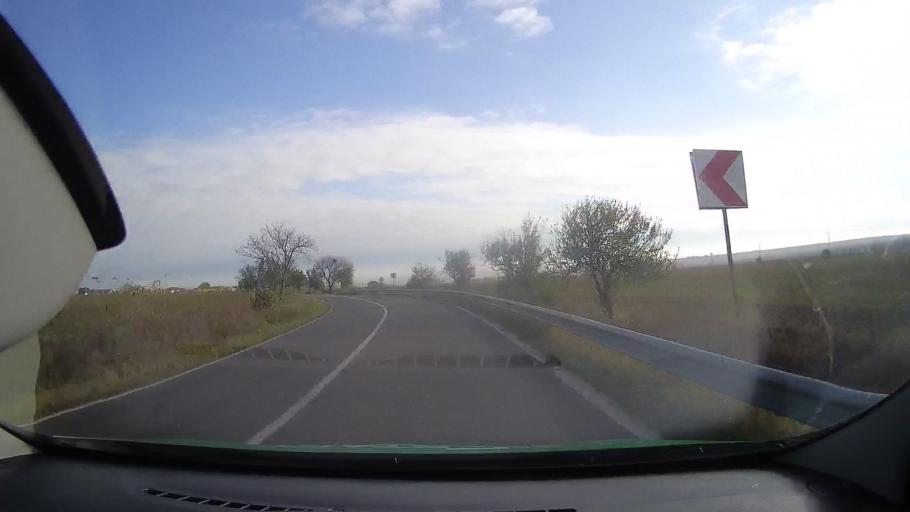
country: RO
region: Tulcea
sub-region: Comuna Mahmudia
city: Mahmudia
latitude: 45.0773
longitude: 29.0732
